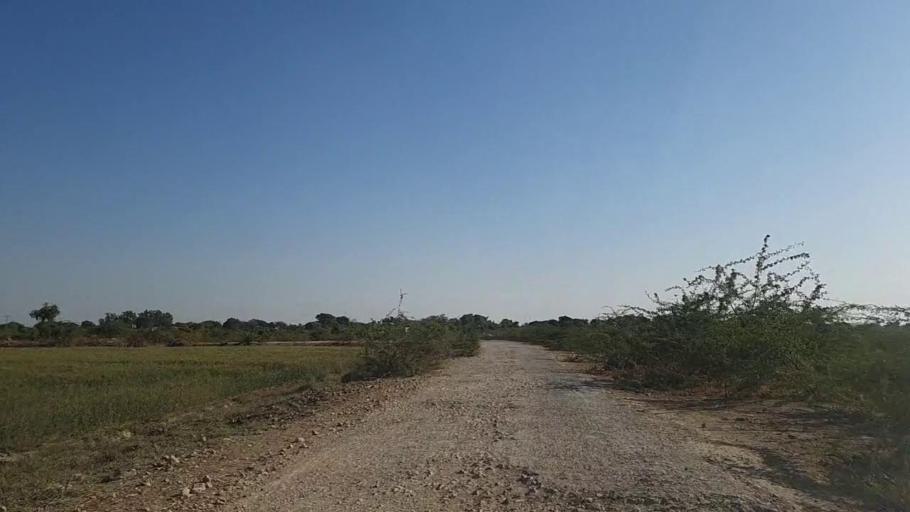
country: PK
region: Sindh
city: Naukot
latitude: 24.9507
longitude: 69.3284
